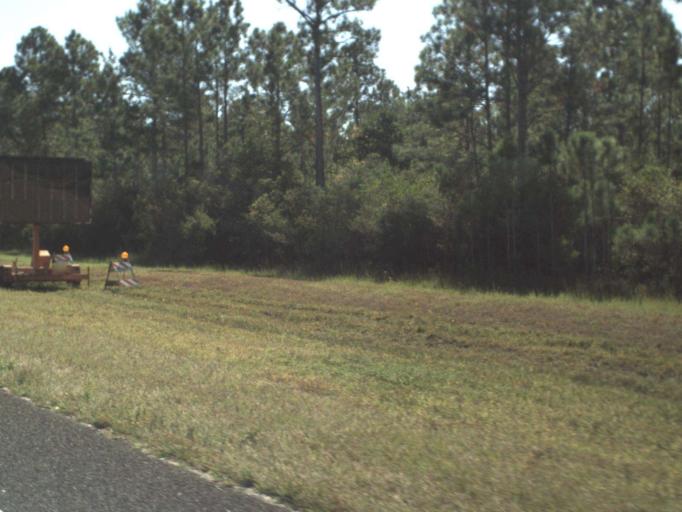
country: US
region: Florida
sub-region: Walton County
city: Seaside
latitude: 30.3714
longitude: -86.2036
